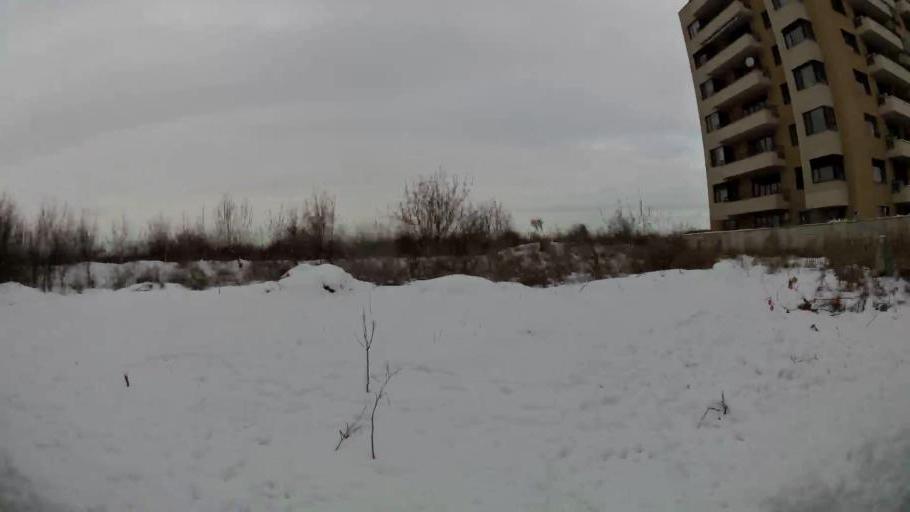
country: RO
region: Ilfov
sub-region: Comuna Otopeni
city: Otopeni
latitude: 44.5113
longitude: 26.1033
